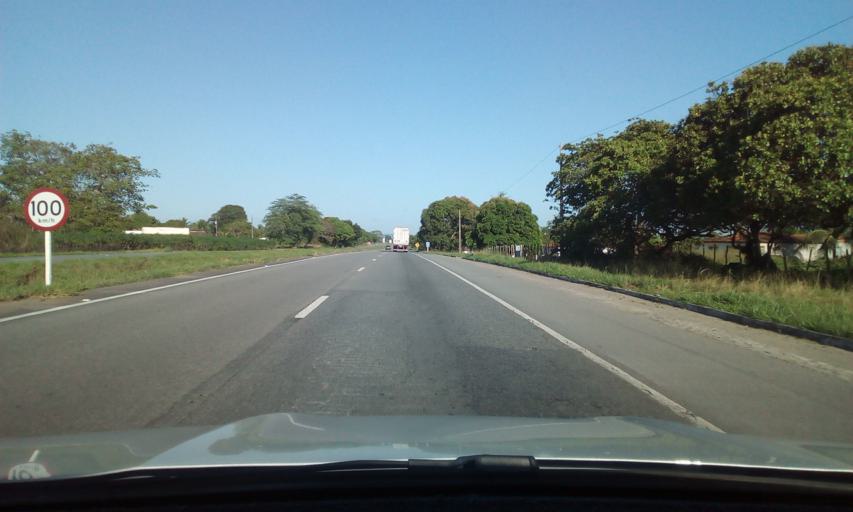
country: BR
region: Paraiba
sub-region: Pilar
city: Pilar
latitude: -7.1868
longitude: -35.2873
